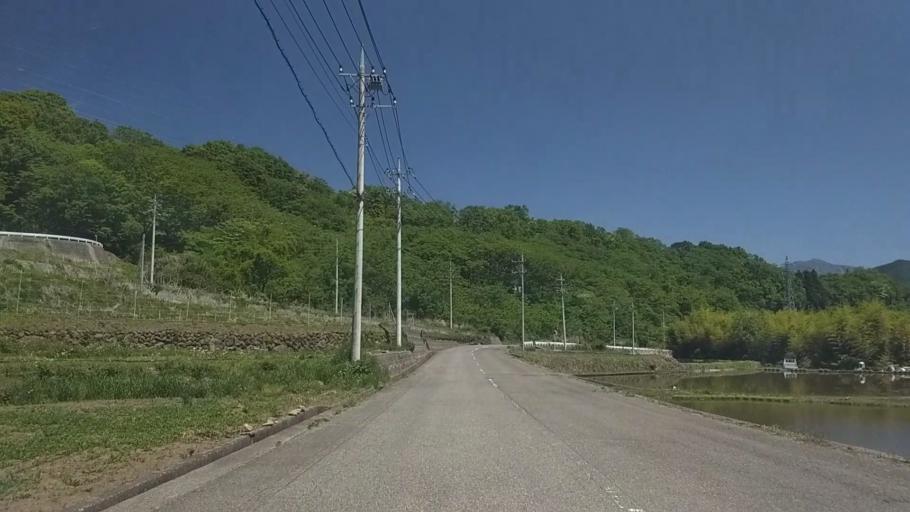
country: JP
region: Yamanashi
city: Nirasaki
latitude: 35.8549
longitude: 138.4338
